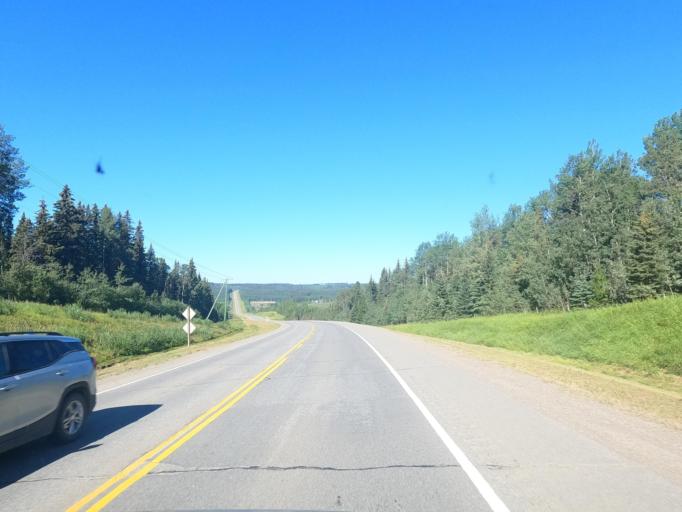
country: CA
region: British Columbia
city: Fort St. John
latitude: 56.6299
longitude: -121.5189
